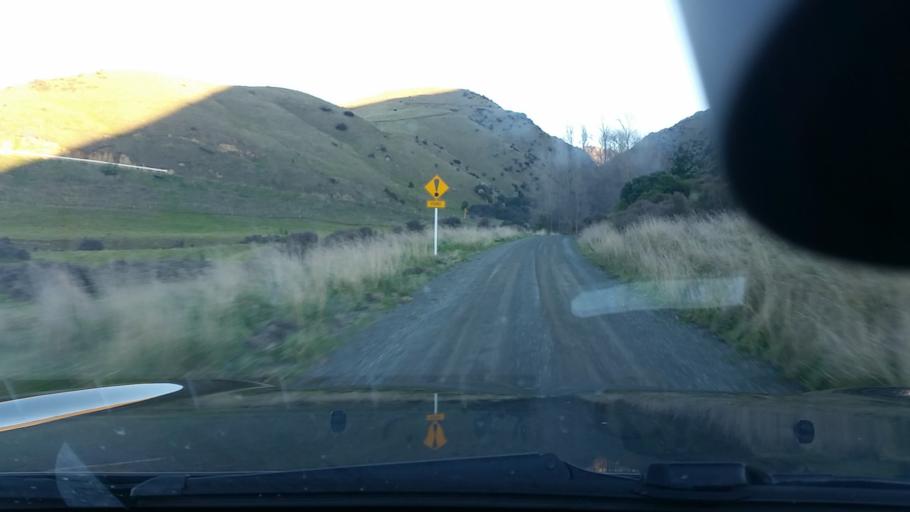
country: NZ
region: Marlborough
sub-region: Marlborough District
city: Blenheim
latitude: -41.7470
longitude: 174.0563
